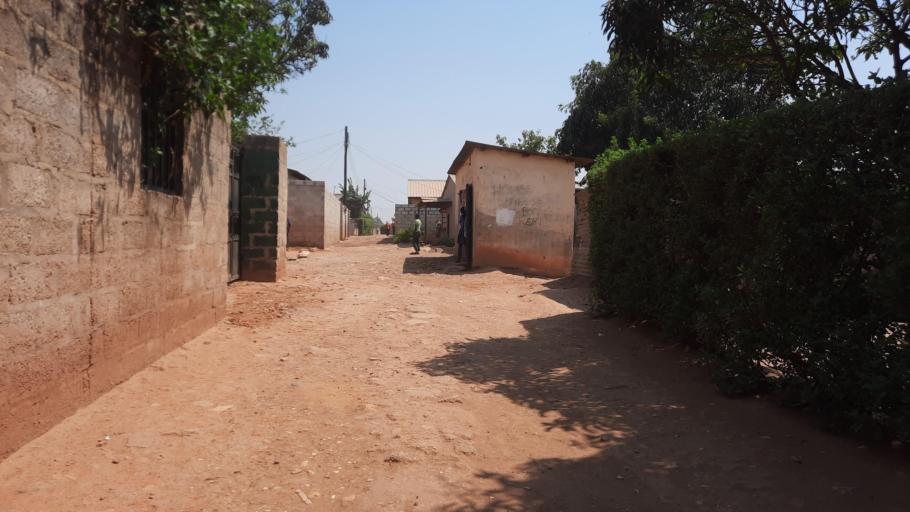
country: ZM
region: Lusaka
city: Lusaka
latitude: -15.3978
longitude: 28.3747
